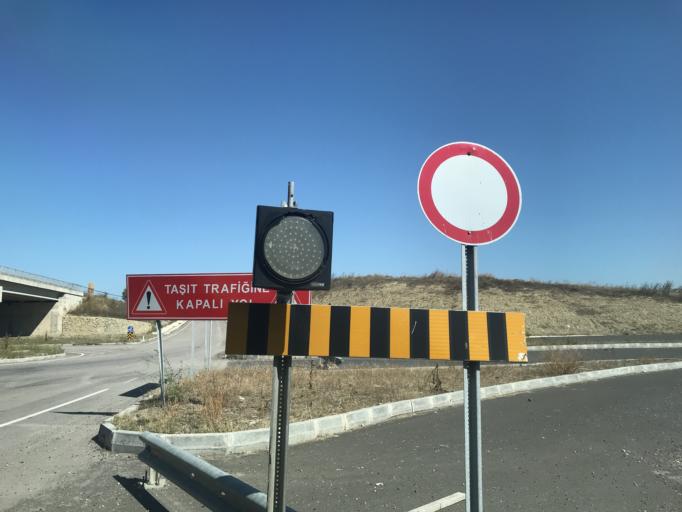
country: TR
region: Tekirdag
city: Kumbag
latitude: 40.9431
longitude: 27.4338
